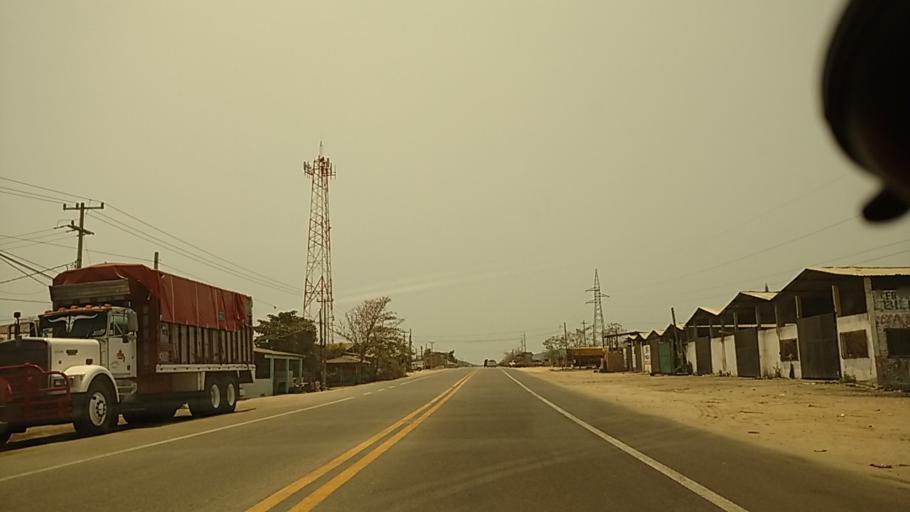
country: MX
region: Guerrero
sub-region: Tecpan de Galeana
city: Villa Rotaria
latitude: 17.2726
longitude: -100.9501
